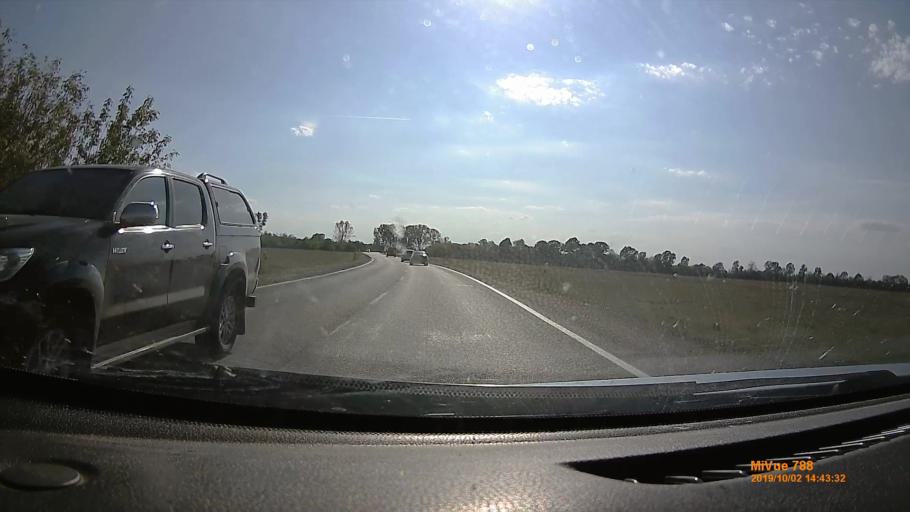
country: HU
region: Heves
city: Szihalom
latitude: 47.7739
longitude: 20.4633
